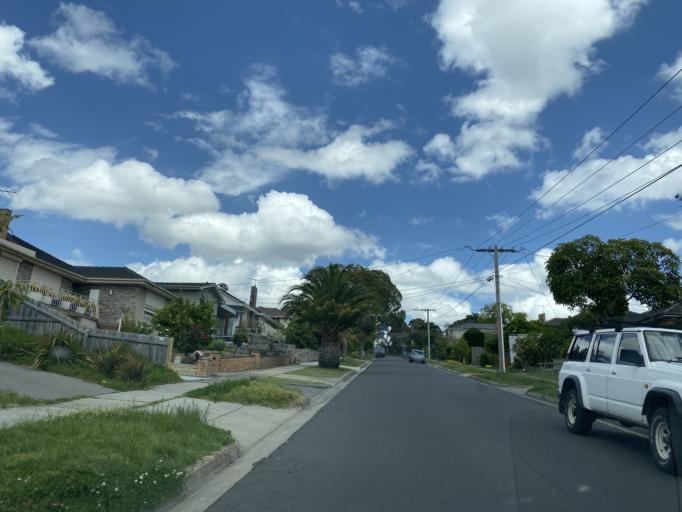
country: AU
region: Victoria
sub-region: Whitehorse
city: Burwood
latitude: -37.8577
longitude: 145.1235
